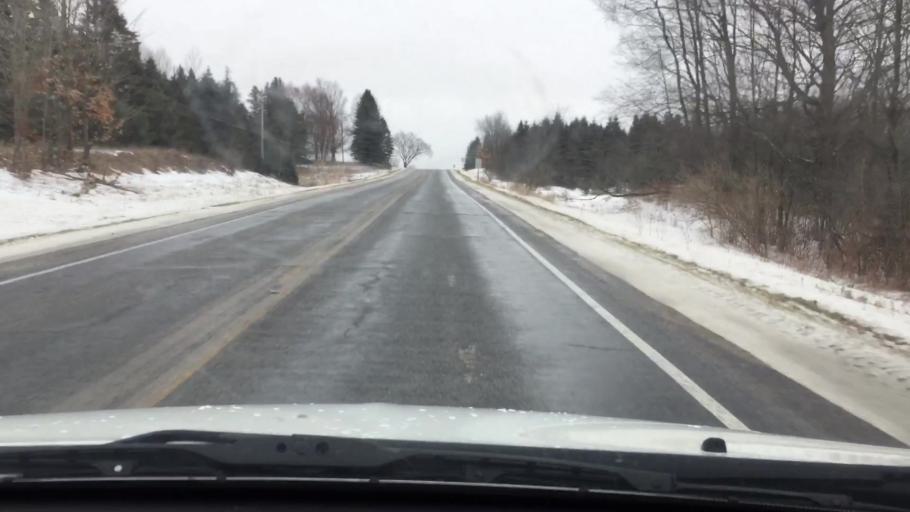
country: US
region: Michigan
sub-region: Osceola County
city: Reed City
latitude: 44.0476
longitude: -85.4439
